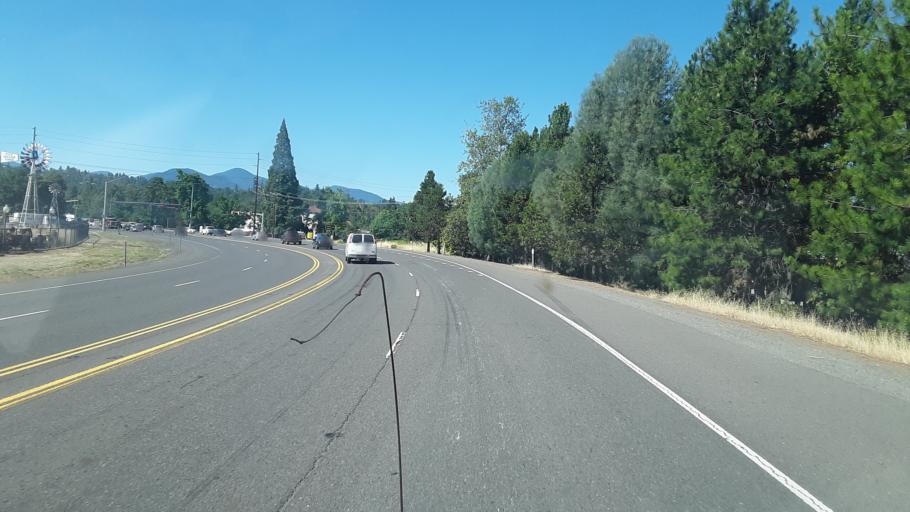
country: US
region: Oregon
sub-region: Josephine County
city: Fruitdale
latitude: 42.4326
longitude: -123.3171
